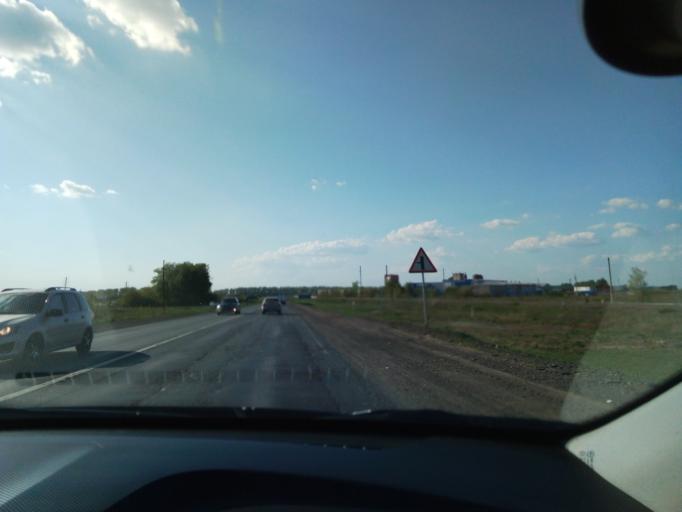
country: RU
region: Chuvashia
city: Novyye Lapsary
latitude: 56.0675
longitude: 47.2351
